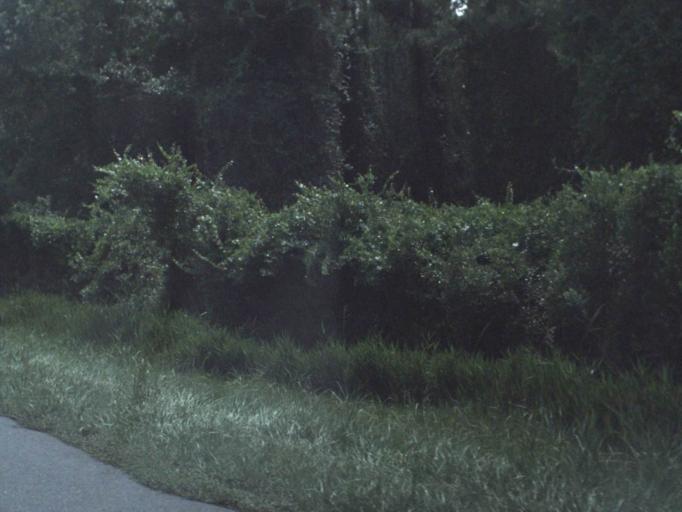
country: US
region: Florida
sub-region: Hamilton County
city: Jasper
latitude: 30.5855
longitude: -82.6789
